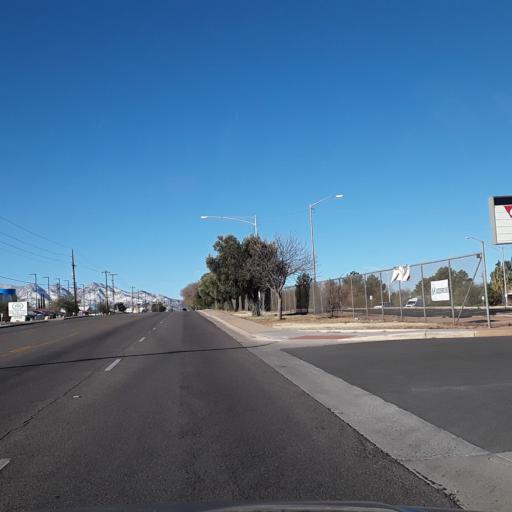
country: US
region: Arizona
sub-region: Cochise County
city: Sierra Vista
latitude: 31.5547
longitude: -110.2634
